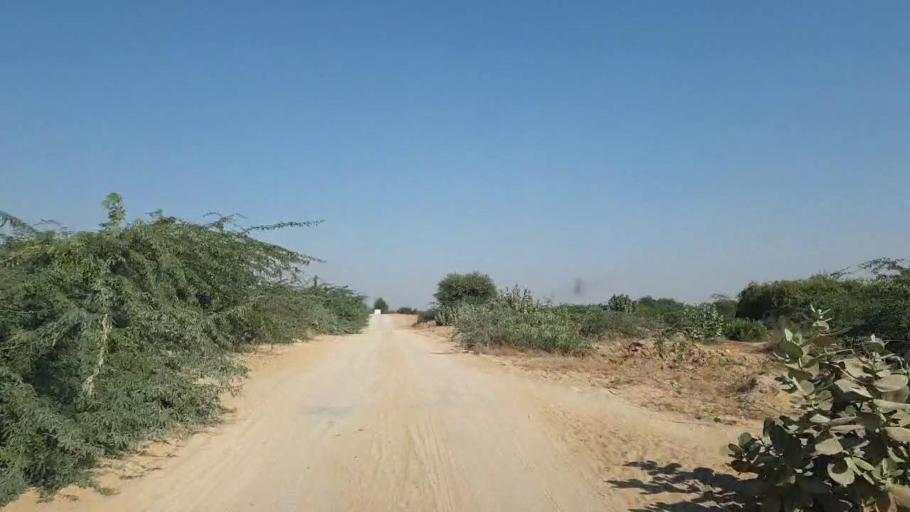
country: PK
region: Sindh
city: Gharo
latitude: 25.1776
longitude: 67.7342
